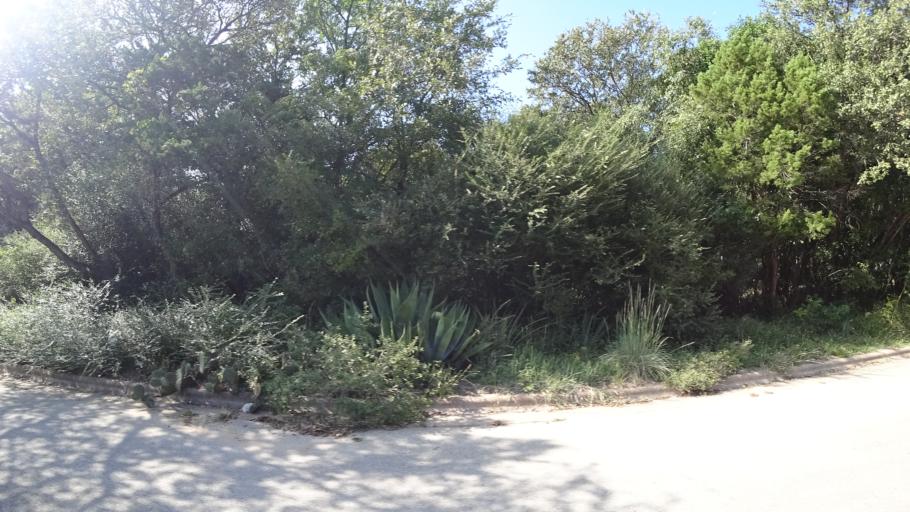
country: US
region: Texas
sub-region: Travis County
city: Rollingwood
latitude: 30.2818
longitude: -97.7963
